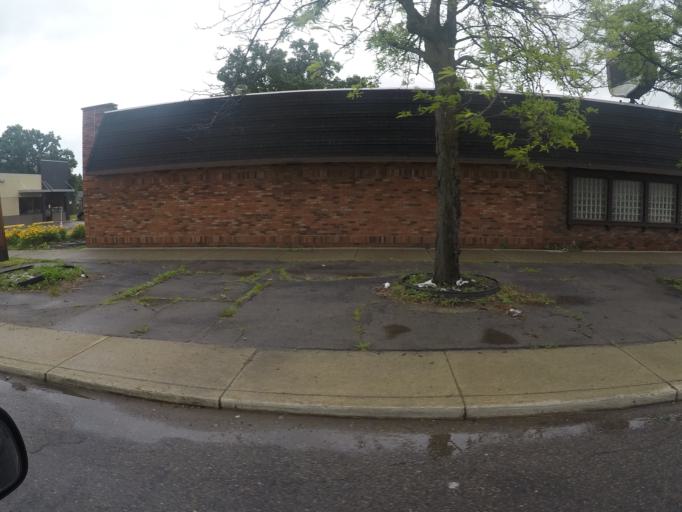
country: US
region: Michigan
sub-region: Wayne County
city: Grosse Pointe
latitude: 42.4075
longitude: -82.9257
